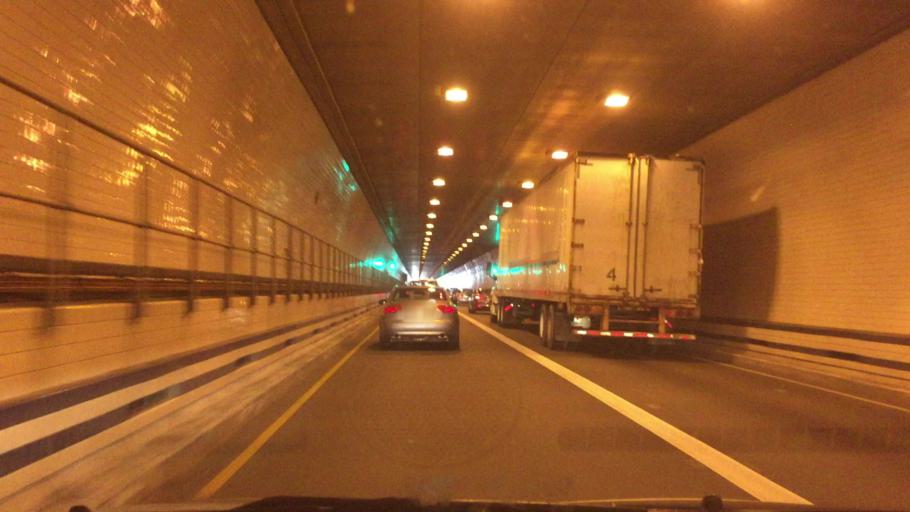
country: US
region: Virginia
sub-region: City of Newport News
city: Newport News
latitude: 36.9520
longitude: -76.4071
